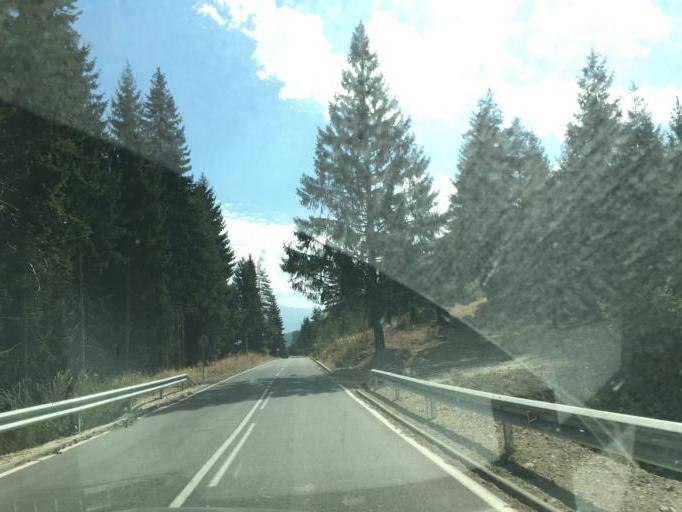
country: BG
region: Pazardzhik
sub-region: Obshtina Batak
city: Batak
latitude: 41.8922
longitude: 24.3225
